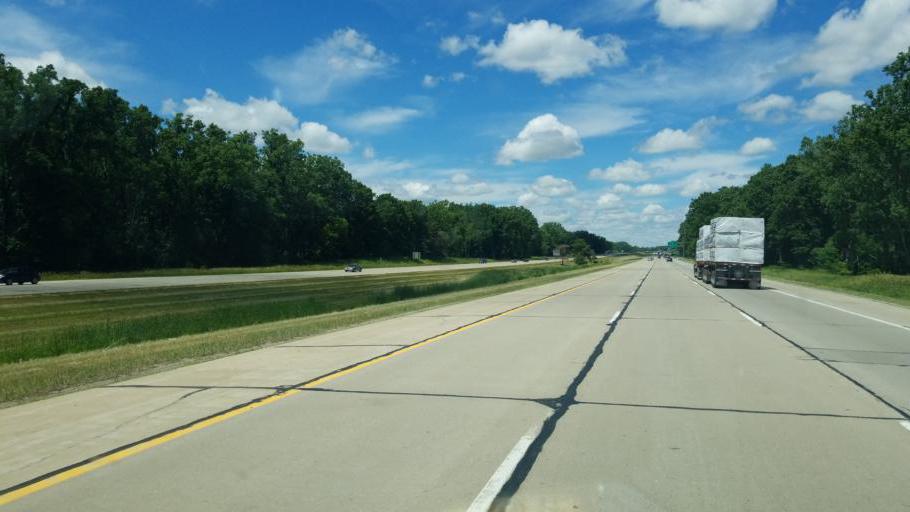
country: US
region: Michigan
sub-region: Livingston County
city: Howell
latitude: 42.6063
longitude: -83.9609
